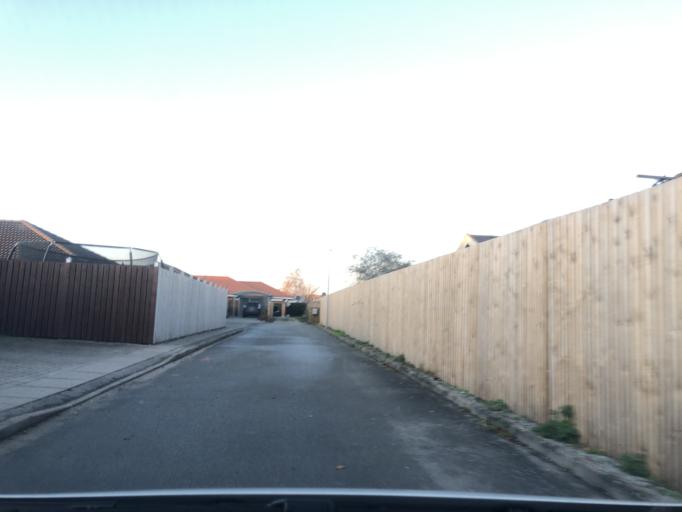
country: DK
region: Capital Region
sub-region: Tarnby Kommune
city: Tarnby
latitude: 55.6000
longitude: 12.5807
